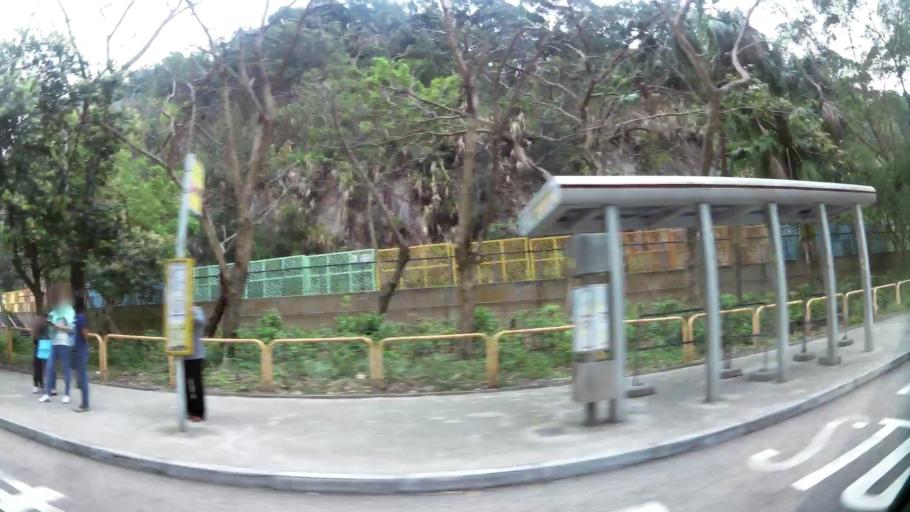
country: HK
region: Kowloon City
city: Kowloon
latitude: 22.3069
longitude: 114.2389
